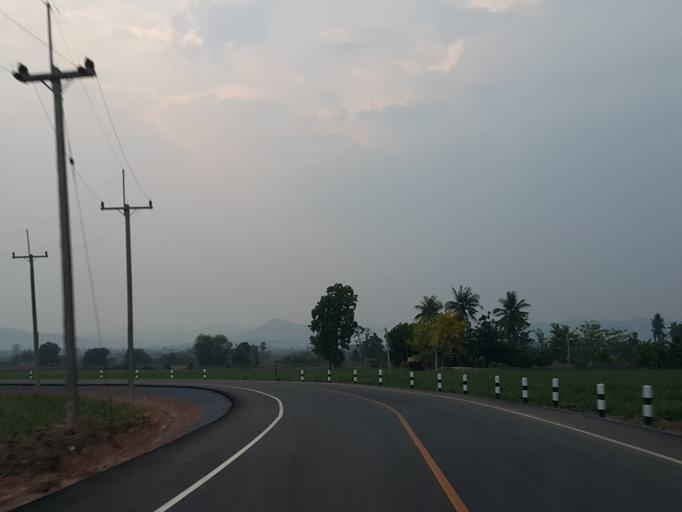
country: TH
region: Suphan Buri
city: Dan Chang
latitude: 14.9392
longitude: 99.6415
